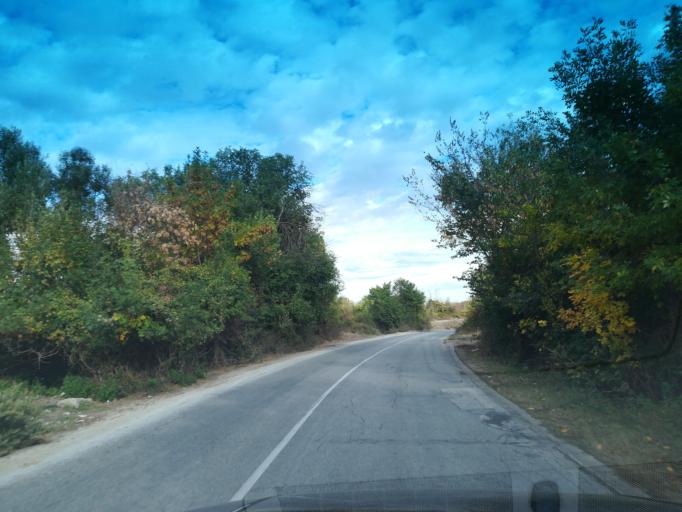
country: BG
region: Pazardzhik
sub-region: Obshtina Peshtera
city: Peshtera
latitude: 42.0498
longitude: 24.3173
